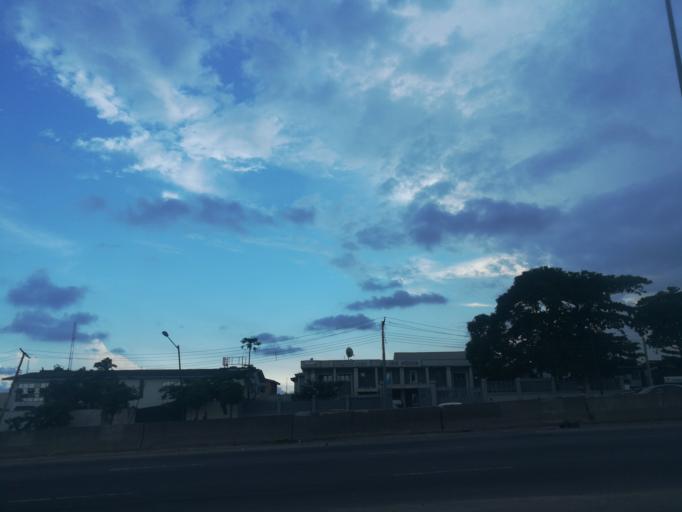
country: NG
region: Lagos
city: Somolu
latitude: 6.5566
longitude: 3.3710
